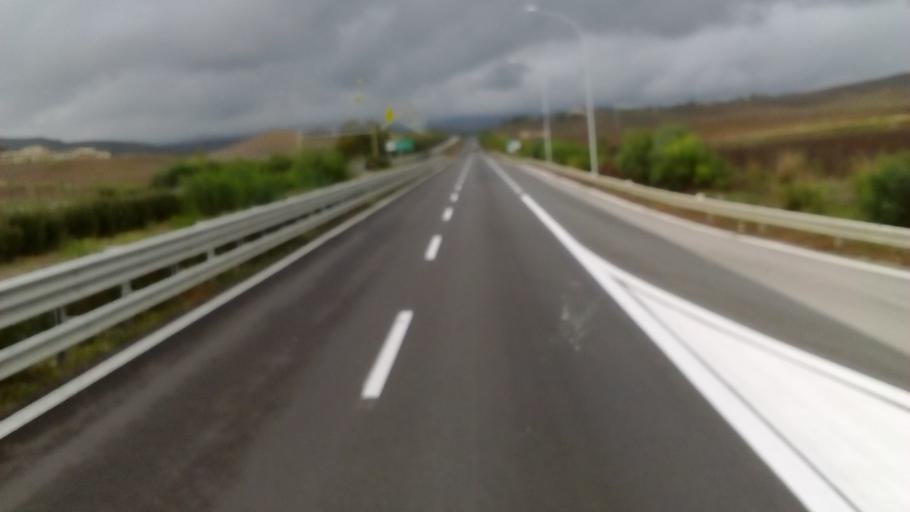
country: IT
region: Sicily
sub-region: Enna
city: Assoro
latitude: 37.5649
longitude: 14.3986
